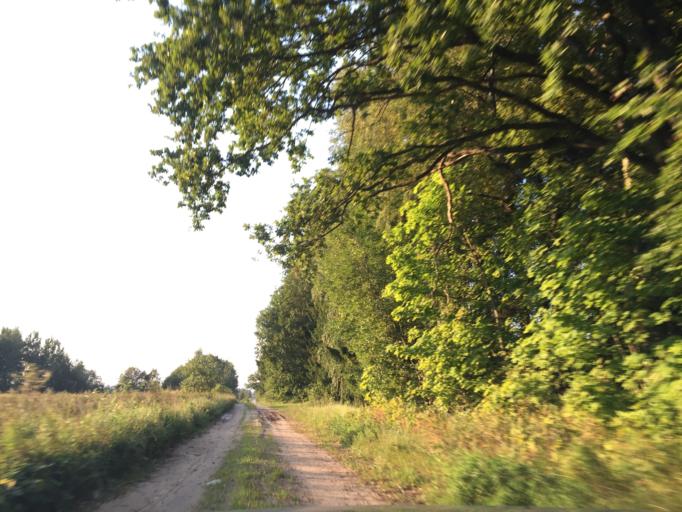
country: LV
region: Limbazu Rajons
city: Limbazi
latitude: 57.5642
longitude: 24.7731
